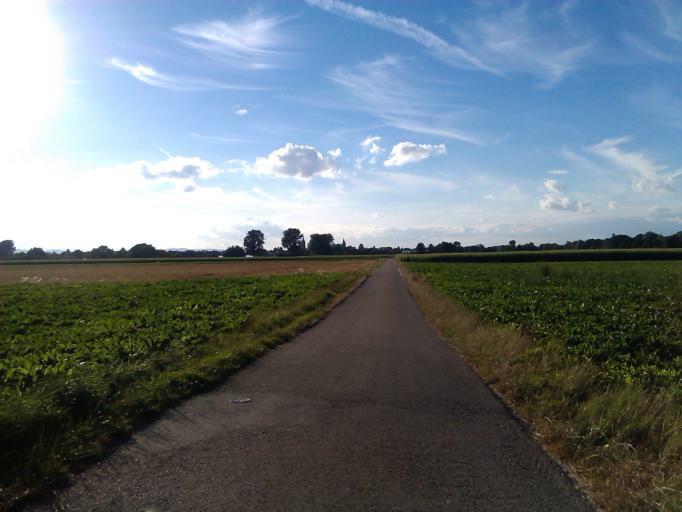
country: DE
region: Rheinland-Pfalz
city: Otterstadt
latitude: 49.3651
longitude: 8.4680
